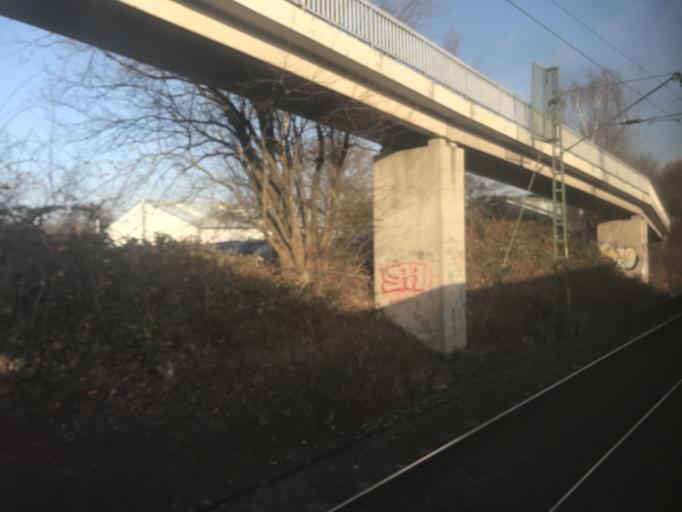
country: DE
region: North Rhine-Westphalia
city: Witten
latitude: 51.5024
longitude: 7.3755
